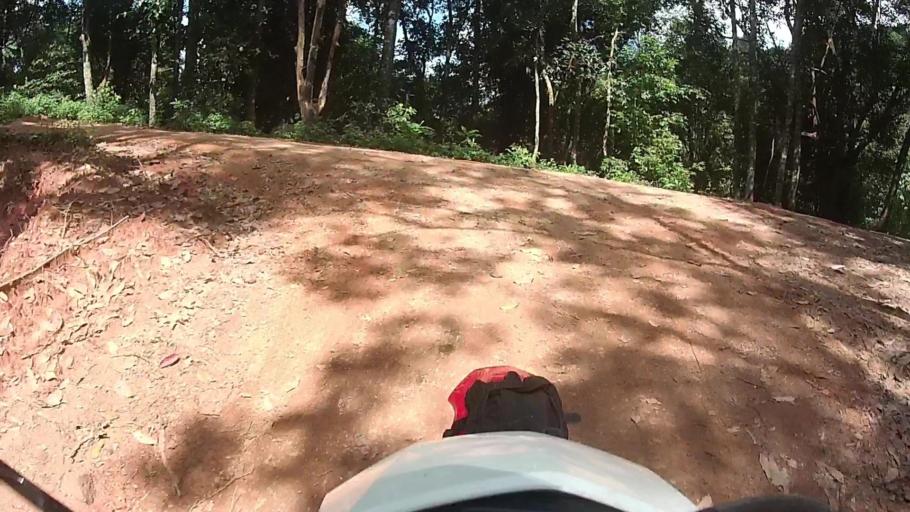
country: TH
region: Chiang Mai
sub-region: Amphoe Chiang Dao
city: Chiang Dao
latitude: 19.3297
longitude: 98.8409
